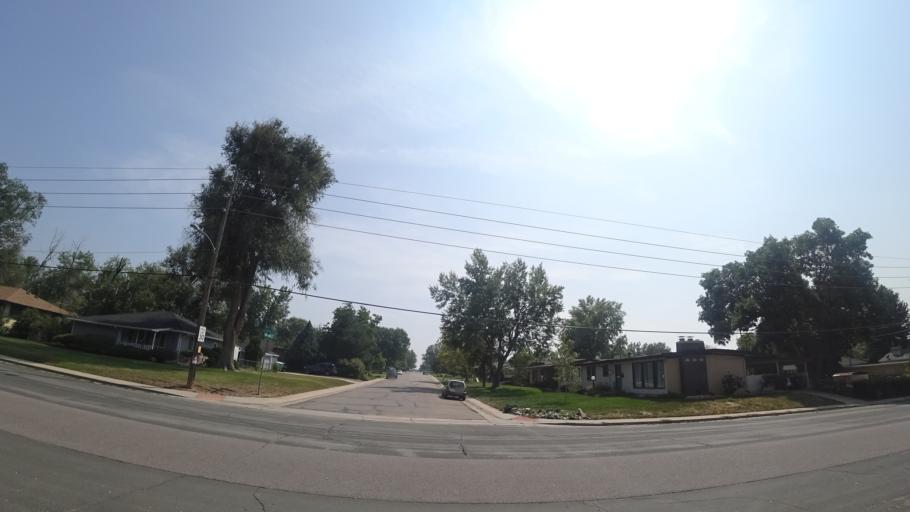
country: US
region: Colorado
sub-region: Arapahoe County
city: Englewood
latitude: 39.6332
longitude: -105.0008
